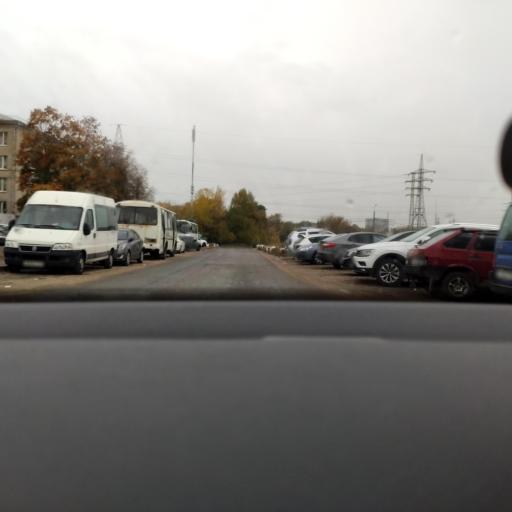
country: RU
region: Moscow
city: Mikhalkovo
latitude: 55.6984
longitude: 37.4332
